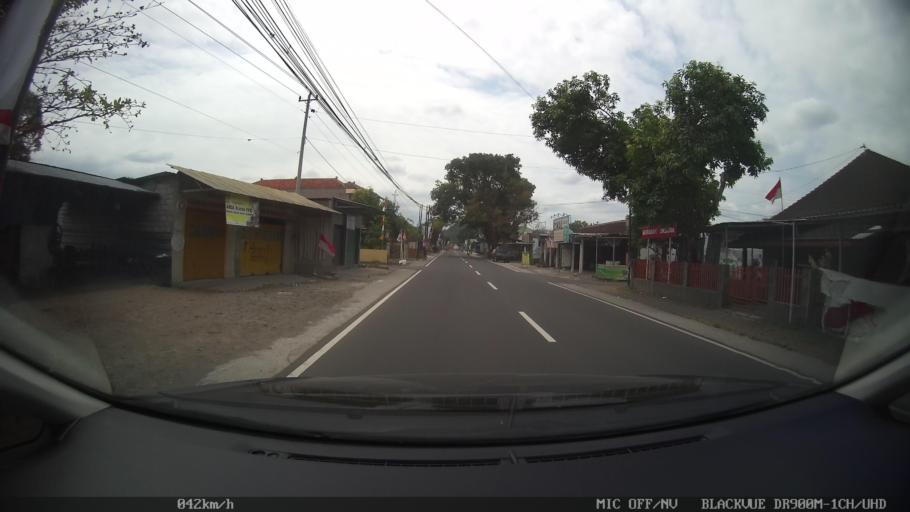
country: ID
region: Central Java
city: Candi Prambanan
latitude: -7.7876
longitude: 110.4827
